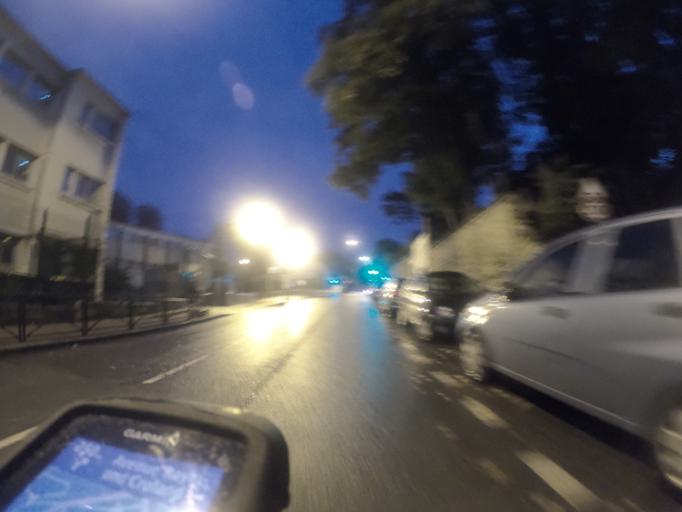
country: FR
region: Ile-de-France
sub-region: Departement des Hauts-de-Seine
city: Fontenay-aux-Roses
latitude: 48.7889
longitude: 2.2845
